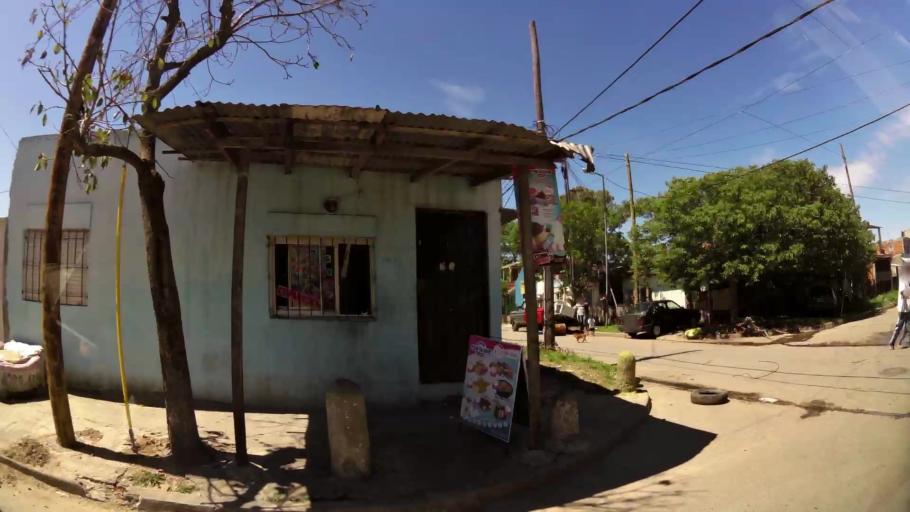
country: AR
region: Buenos Aires
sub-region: Partido de Lanus
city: Lanus
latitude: -34.7282
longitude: -58.3364
